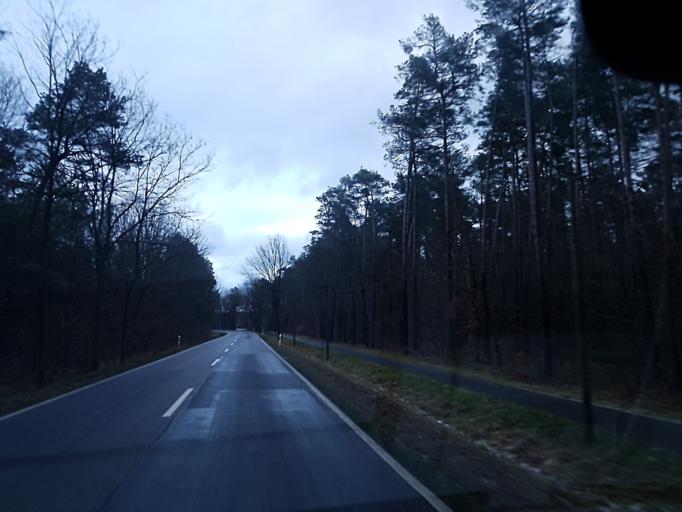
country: DE
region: Brandenburg
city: Finsterwalde
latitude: 51.5815
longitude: 13.6982
